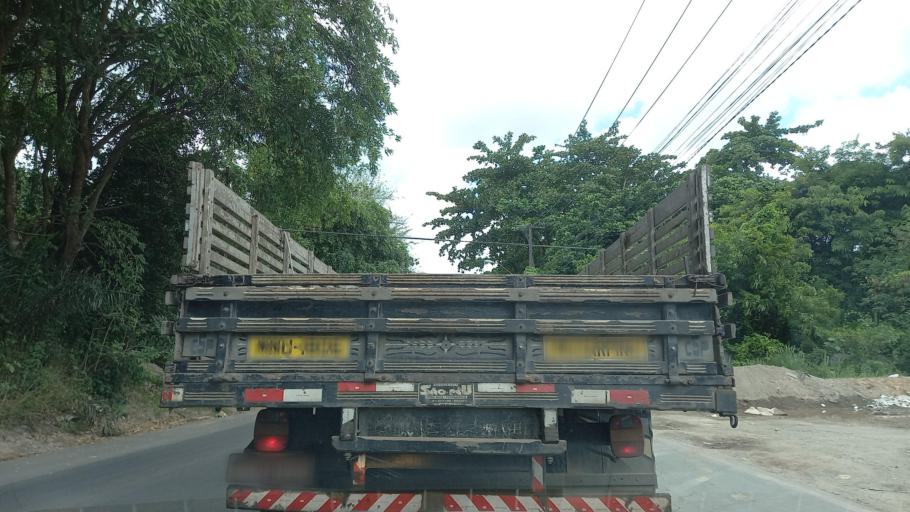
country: BR
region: Pernambuco
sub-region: Jaboatao Dos Guararapes
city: Jaboatao dos Guararapes
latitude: -8.1121
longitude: -35.0071
